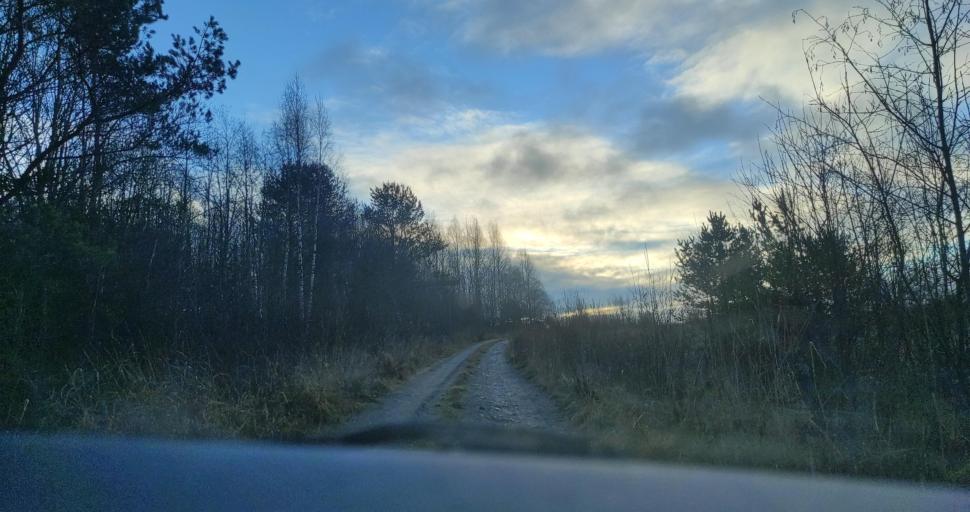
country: RU
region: Republic of Karelia
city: Pitkyaranta
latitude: 61.7289
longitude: 31.3813
